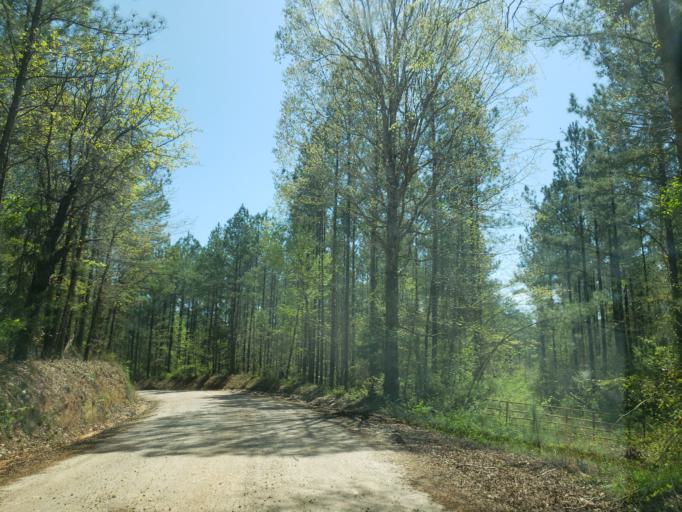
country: US
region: Alabama
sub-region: Lee County
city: Auburn
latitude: 32.6358
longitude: -85.6432
